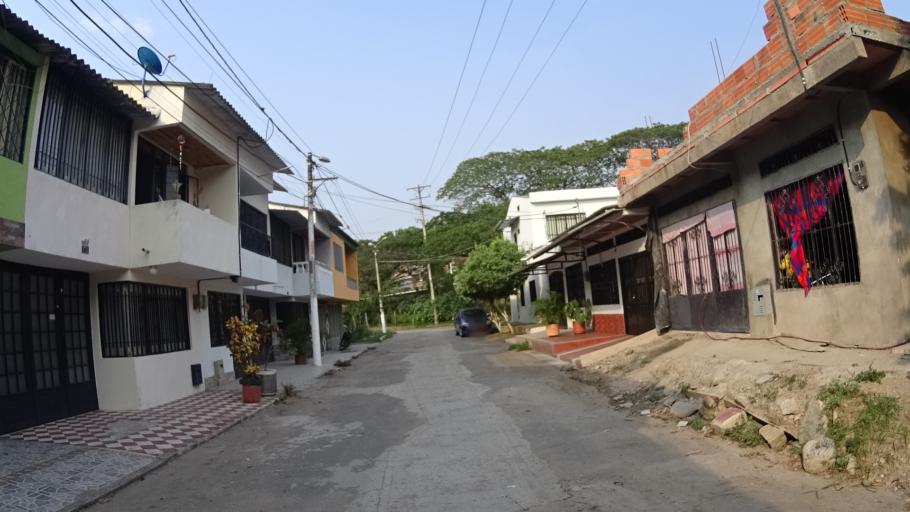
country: CO
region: Cundinamarca
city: Puerto Salgar
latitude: 5.4718
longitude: -74.6701
